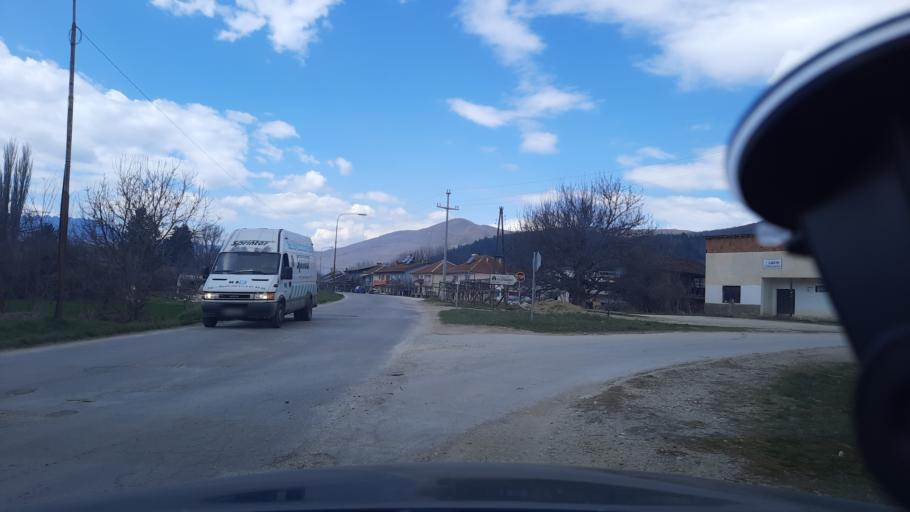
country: MK
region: Demir Hisar
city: Sopotnica
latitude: 41.2929
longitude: 21.1567
